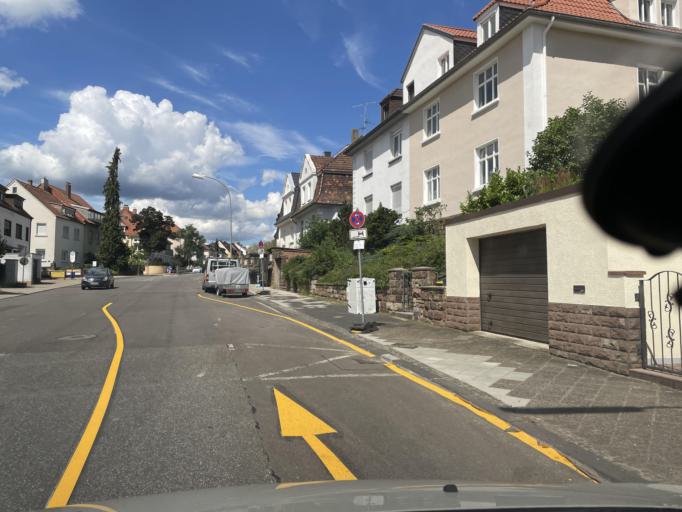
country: DE
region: Saarland
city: Saarbrucken
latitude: 49.2301
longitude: 7.0206
